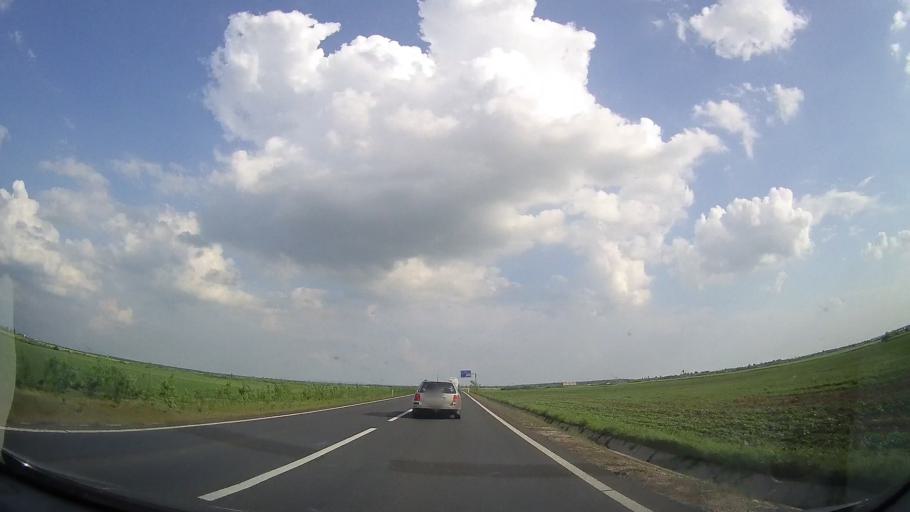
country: RO
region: Timis
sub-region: Comuna Remetea Mare
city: Remetea Mare
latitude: 45.7992
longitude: 21.4123
